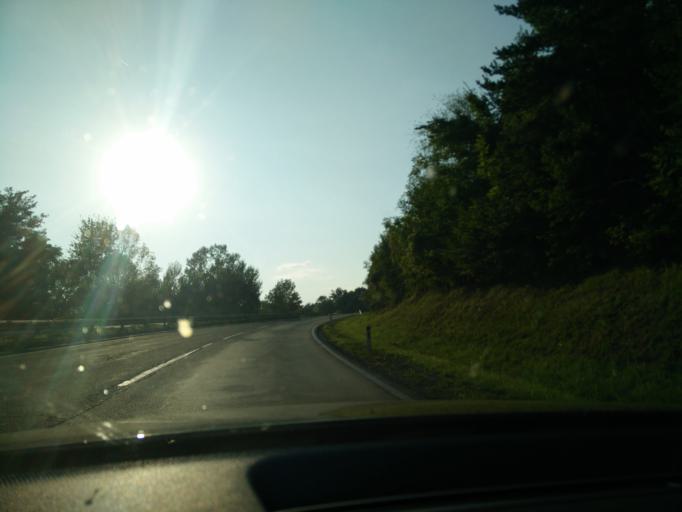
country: AT
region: Carinthia
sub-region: Politischer Bezirk Klagenfurt Land
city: Kottmannsdorf
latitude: 46.5446
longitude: 14.2533
